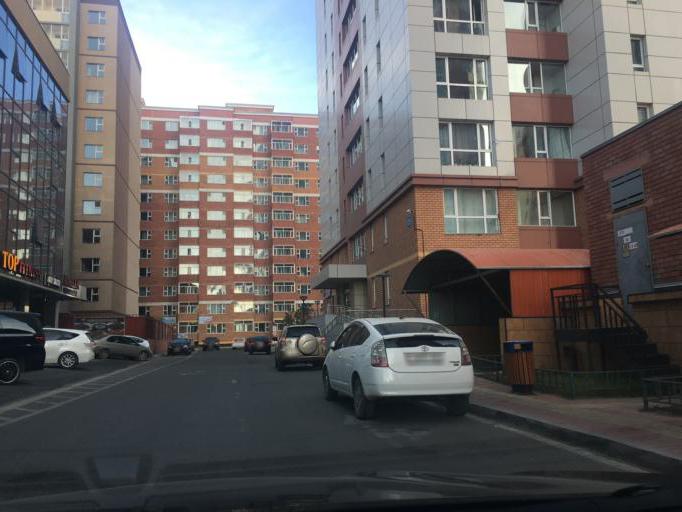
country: MN
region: Ulaanbaatar
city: Ulaanbaatar
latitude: 47.9066
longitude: 106.8984
